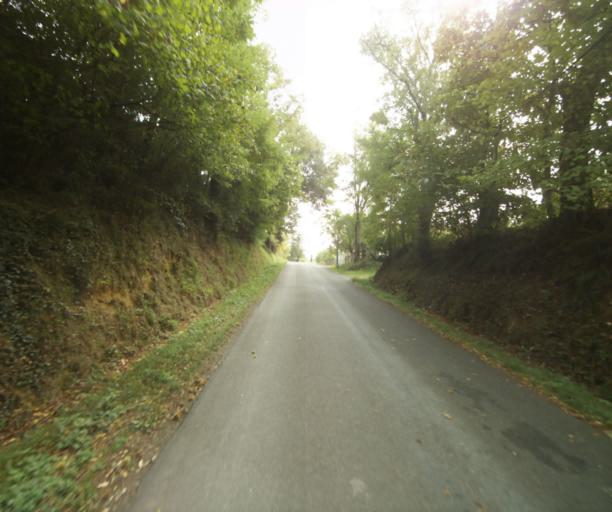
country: FR
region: Midi-Pyrenees
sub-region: Departement du Gers
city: Eauze
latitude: 43.8384
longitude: 0.1135
